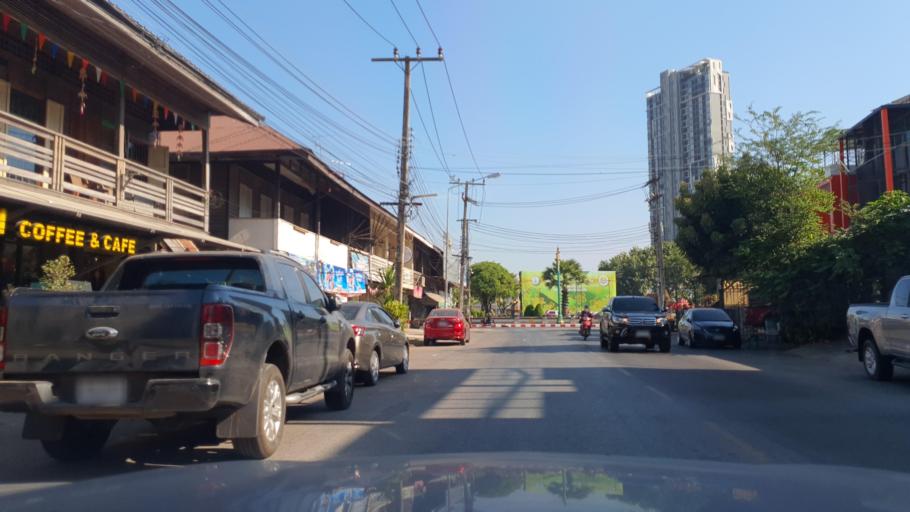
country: TH
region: Khon Kaen
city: Khon Kaen
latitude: 16.4301
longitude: 102.8279
